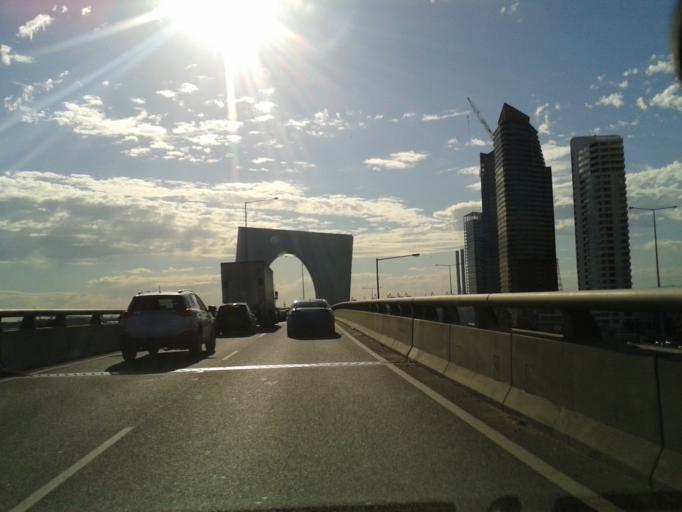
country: AU
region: Victoria
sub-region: Melbourne
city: Docklands
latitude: -37.8268
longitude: 144.9479
